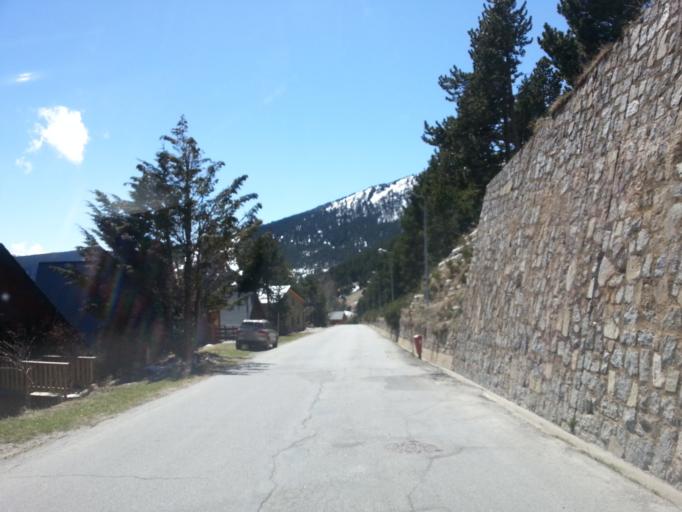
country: ES
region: Catalonia
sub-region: Provincia de Girona
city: Llivia
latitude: 42.5846
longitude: 2.0740
